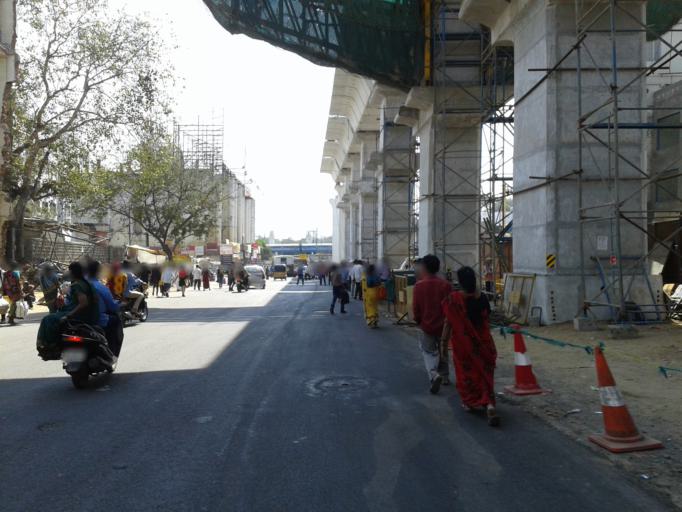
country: IN
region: Telangana
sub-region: Hyderabad
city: Malkajgiri
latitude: 17.4360
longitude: 78.5054
